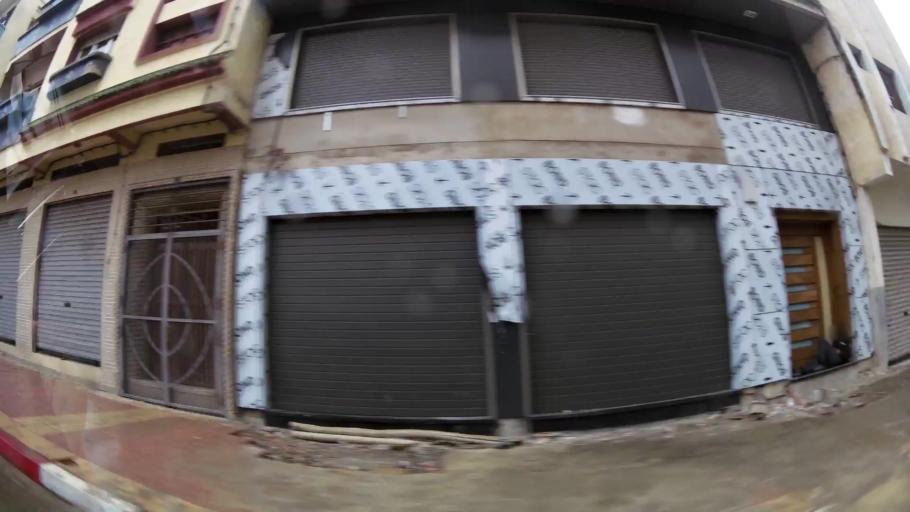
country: MA
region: Taza-Al Hoceima-Taounate
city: Al Hoceima
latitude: 35.2494
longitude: -3.9333
